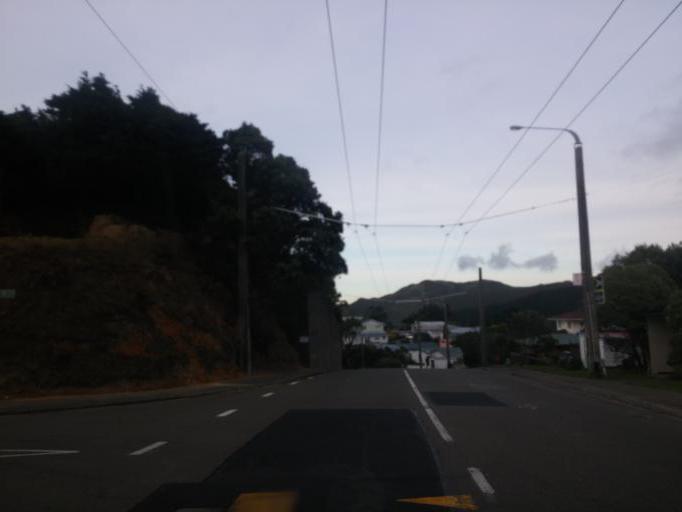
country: NZ
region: Wellington
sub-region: Wellington City
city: Brooklyn
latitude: -41.3208
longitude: 174.7638
